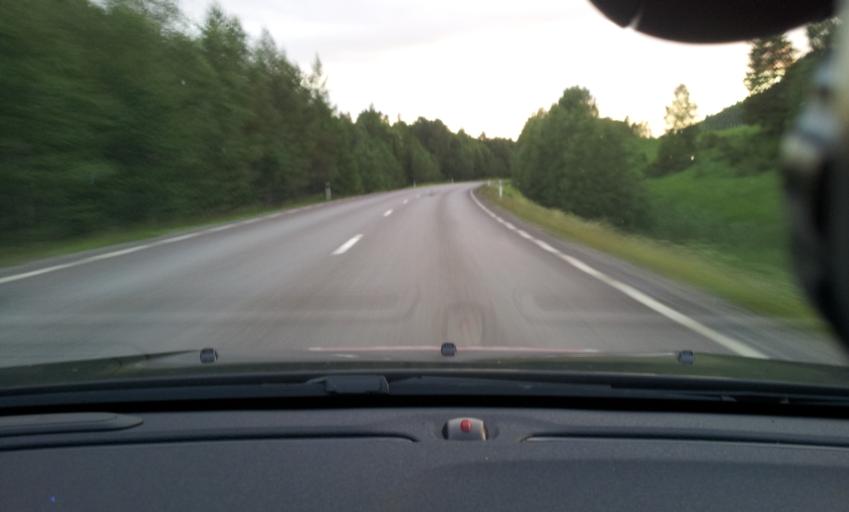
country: SE
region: Jaemtland
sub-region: Ragunda Kommun
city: Hammarstrand
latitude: 63.0922
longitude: 16.4391
